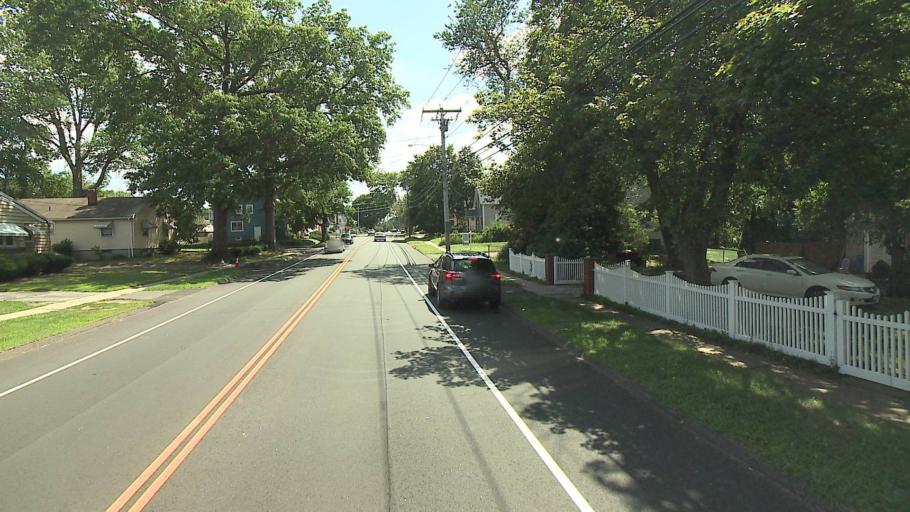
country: US
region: Connecticut
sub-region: Fairfield County
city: Stratford
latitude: 41.2102
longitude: -73.1437
